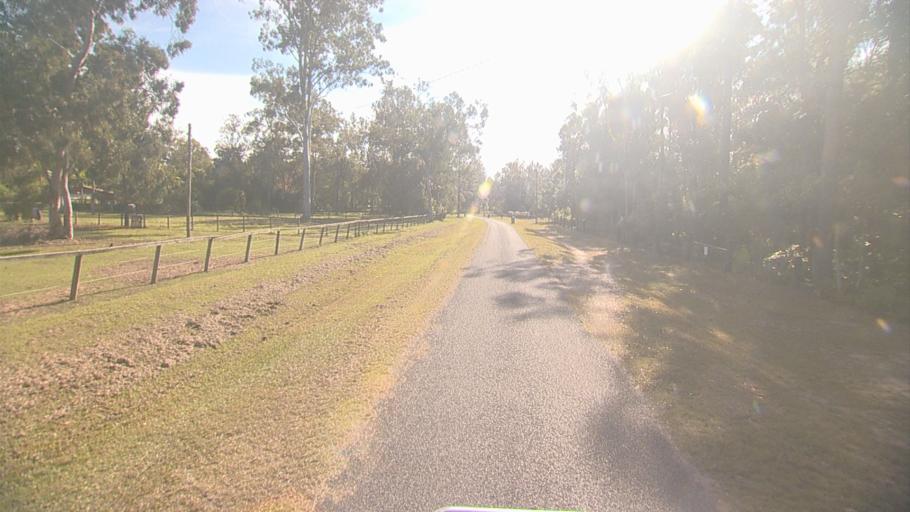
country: AU
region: Queensland
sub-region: Logan
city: Park Ridge South
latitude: -27.7466
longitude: 153.0446
